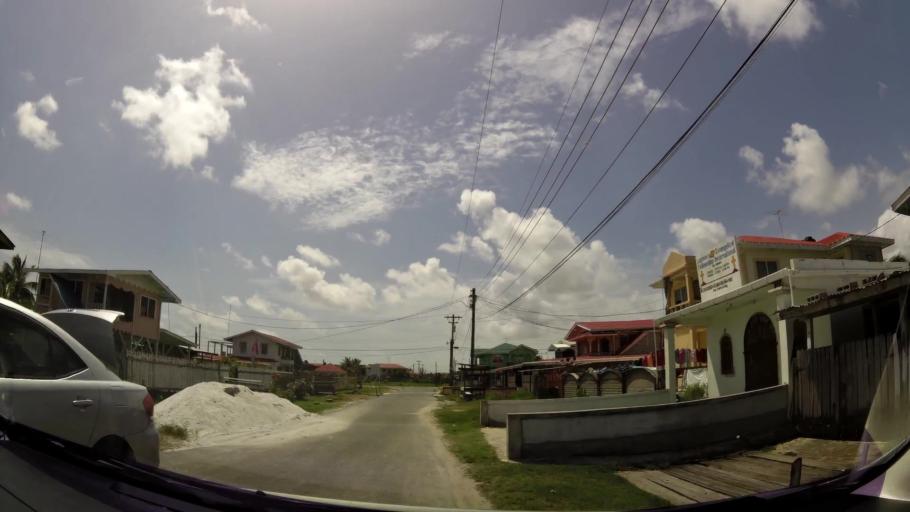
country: GY
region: Demerara-Mahaica
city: Mahaica Village
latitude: 6.7713
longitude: -58.0112
